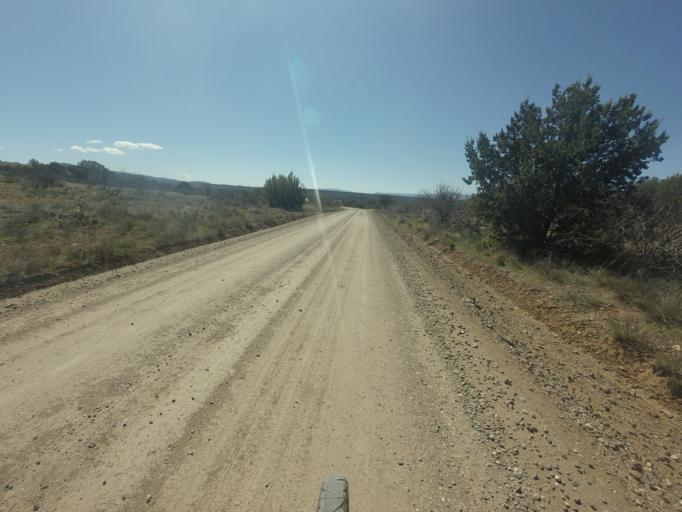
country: US
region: Arizona
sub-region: Yavapai County
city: Lake Montezuma
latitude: 34.6273
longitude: -111.7223
